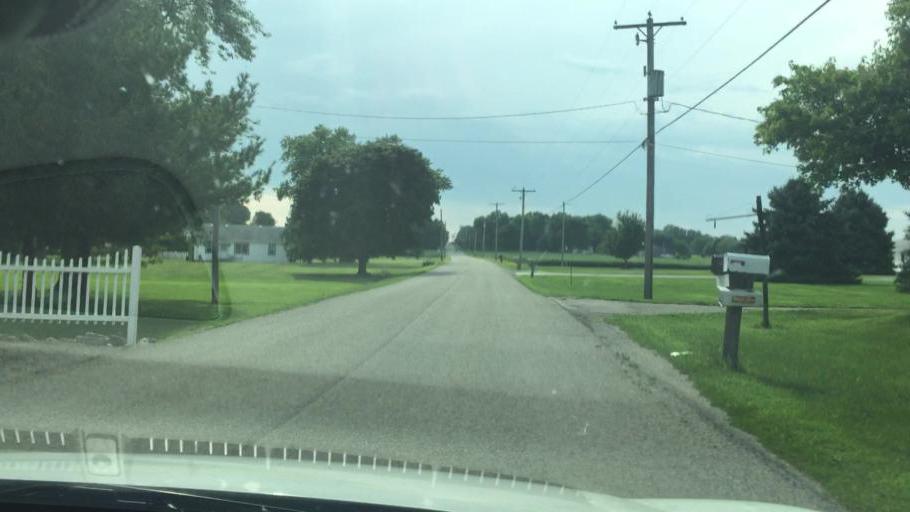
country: US
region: Ohio
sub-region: Clark County
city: Lisbon
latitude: 39.9454
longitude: -83.6002
